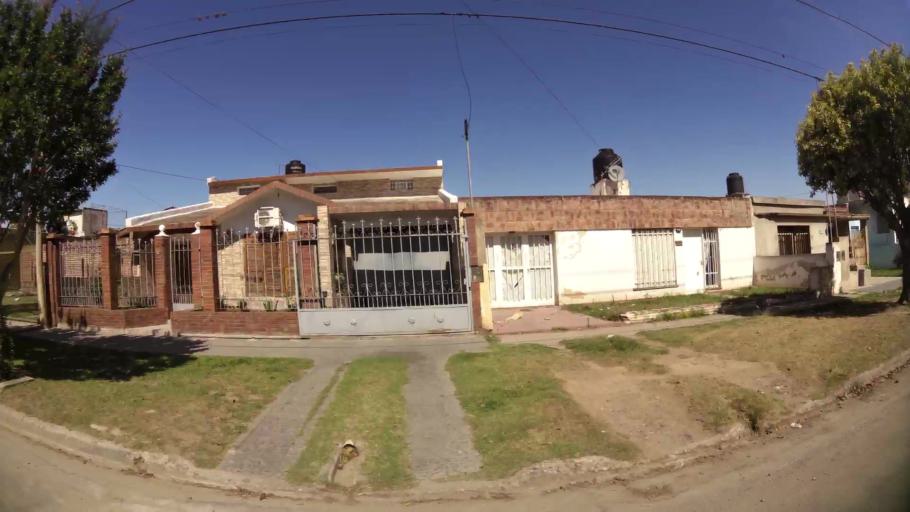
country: AR
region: Cordoba
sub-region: Departamento de Capital
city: Cordoba
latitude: -31.3751
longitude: -64.1673
